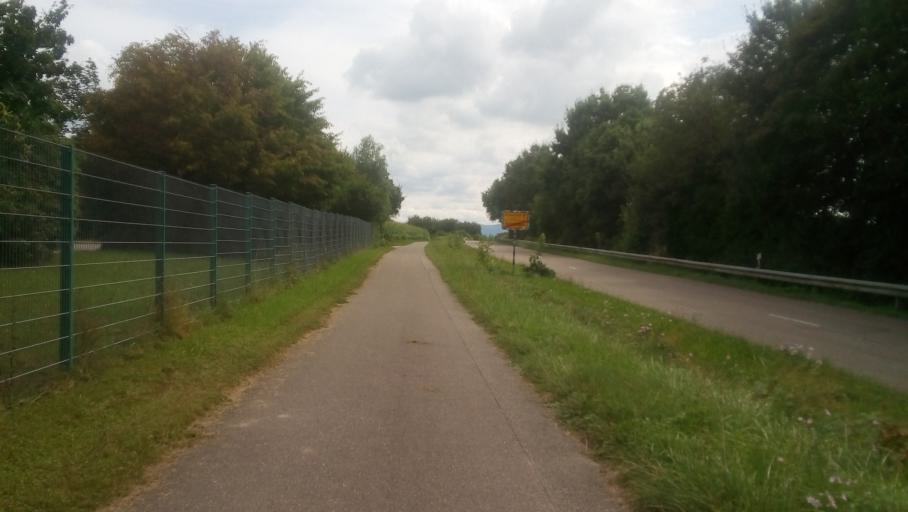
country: DE
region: Baden-Wuerttemberg
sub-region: Karlsruhe Region
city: Lichtenau
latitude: 48.7028
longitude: 7.9749
